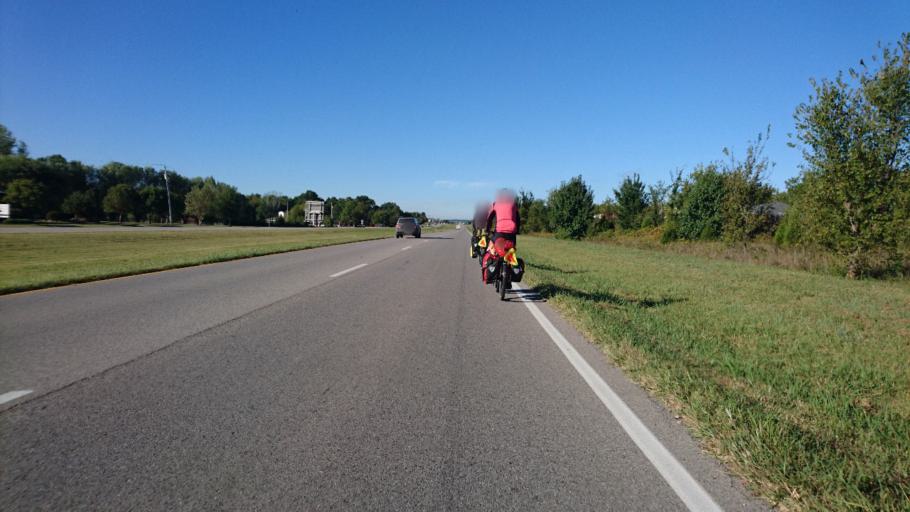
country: US
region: Oklahoma
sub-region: Rogers County
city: Verdigris
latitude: 36.2412
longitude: -95.6788
